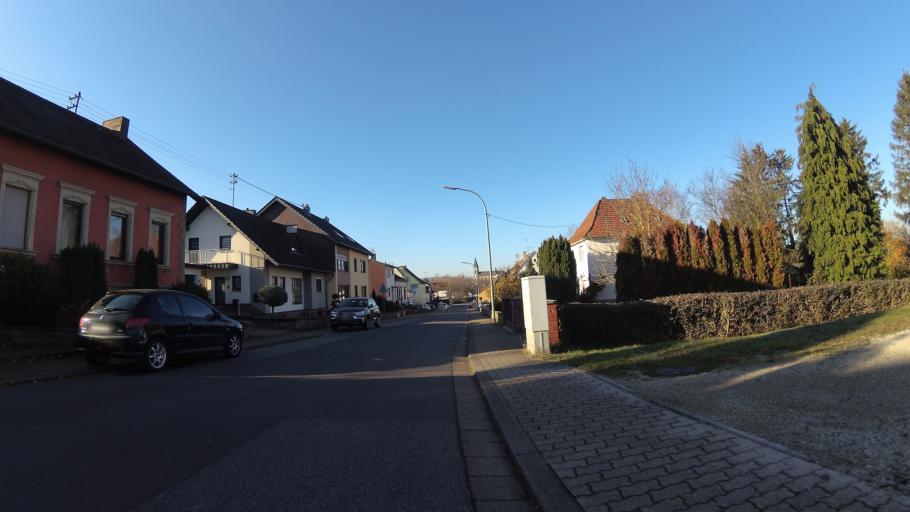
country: DE
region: Saarland
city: Schwalbach
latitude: 49.3002
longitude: 6.8221
